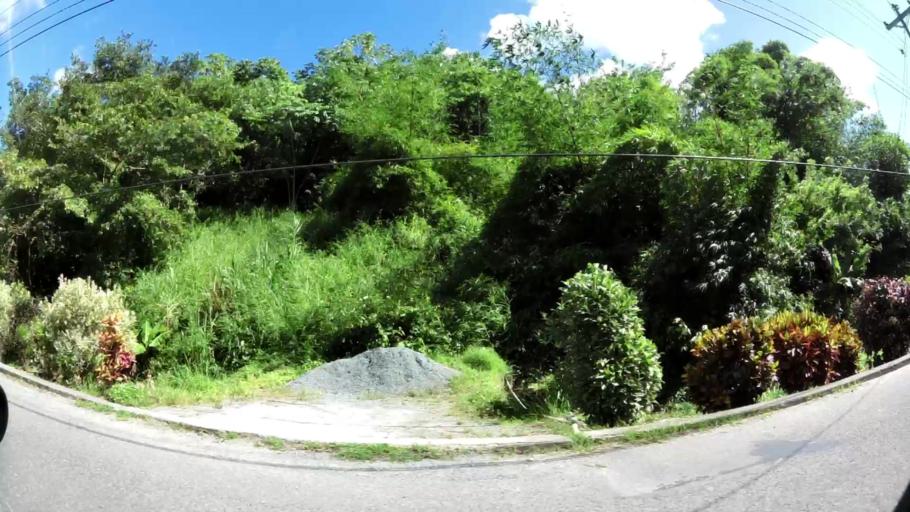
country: TT
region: Tobago
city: Scarborough
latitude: 11.2287
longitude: -60.7411
